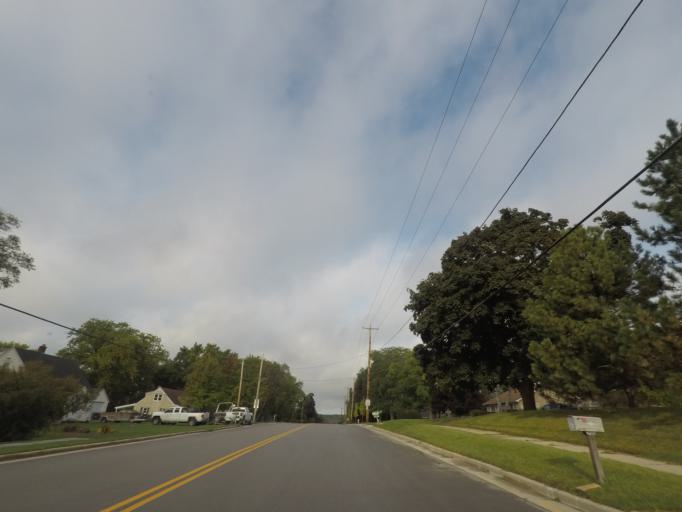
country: US
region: Wisconsin
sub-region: Waukesha County
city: Waukesha
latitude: 43.0321
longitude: -88.2607
